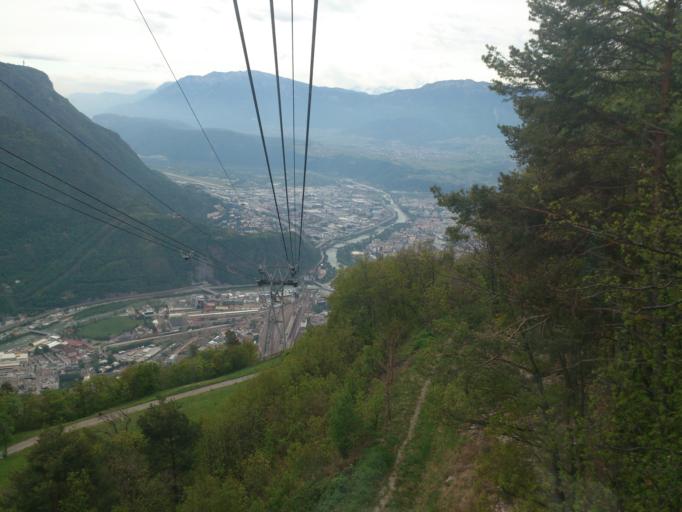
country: IT
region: Trentino-Alto Adige
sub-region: Bolzano
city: Cardano
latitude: 46.5116
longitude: 11.3811
